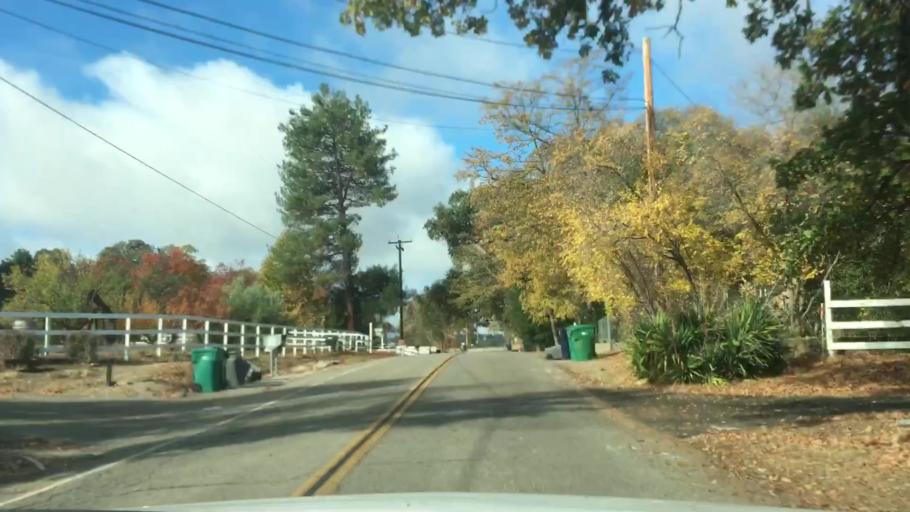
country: US
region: California
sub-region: San Luis Obispo County
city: Atascadero
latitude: 35.4582
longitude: -120.6627
